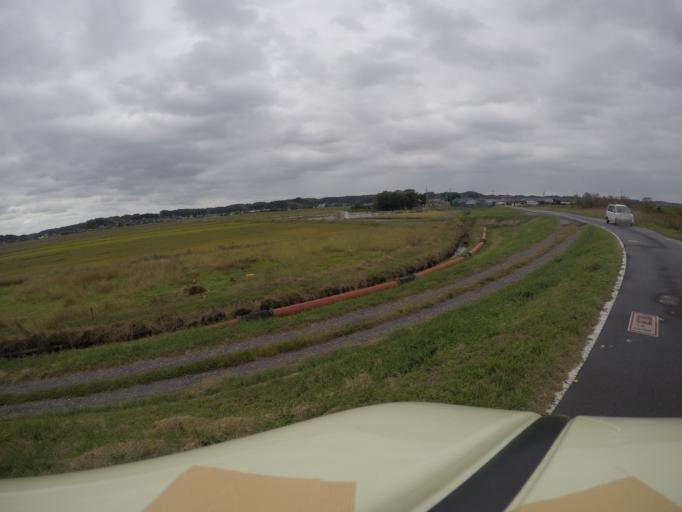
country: JP
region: Ibaraki
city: Itako
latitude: 36.0373
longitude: 140.4465
